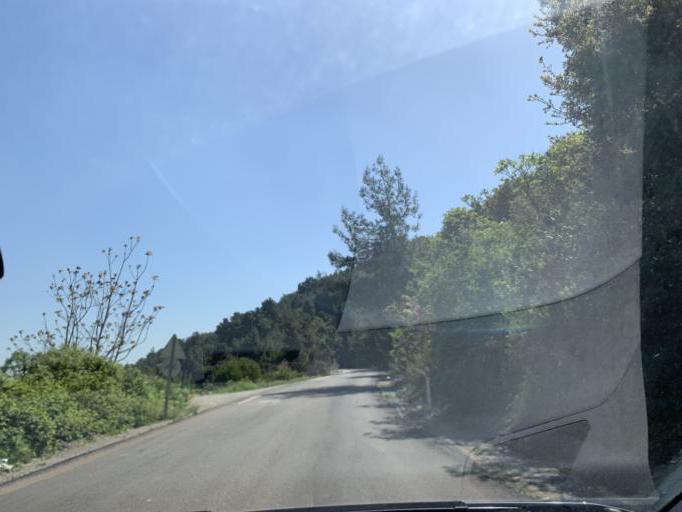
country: TR
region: Bursa
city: Niluefer
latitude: 40.3553
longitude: 28.9782
